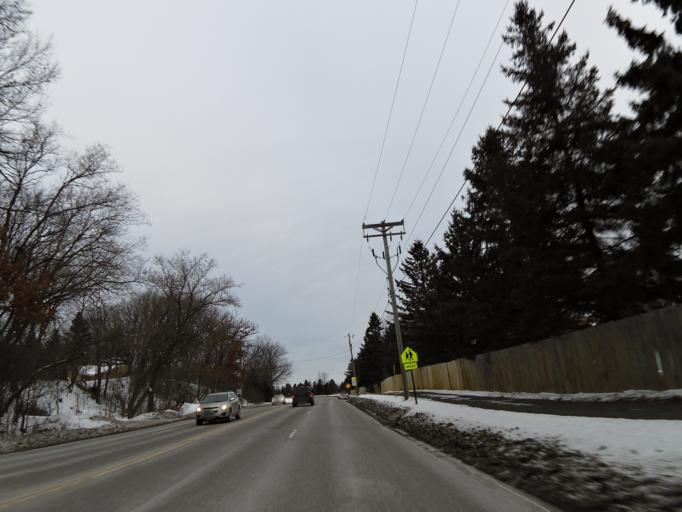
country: US
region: Minnesota
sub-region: Washington County
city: Woodbury
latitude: 44.9032
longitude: -92.9172
